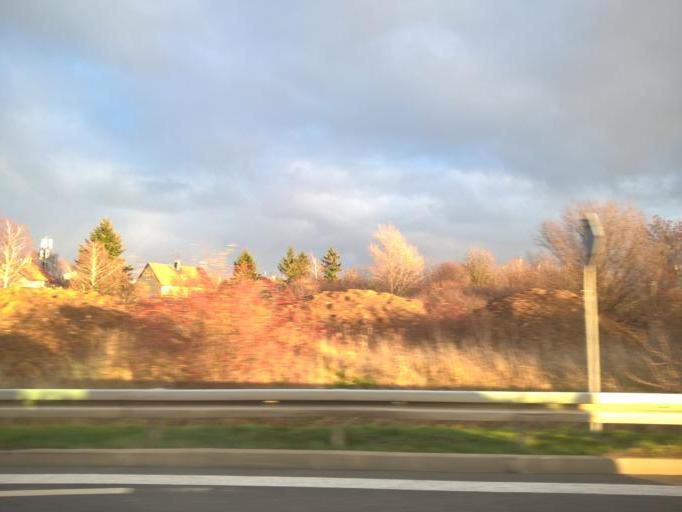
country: CZ
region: Central Bohemia
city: Hostivice
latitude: 50.0927
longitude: 14.2979
